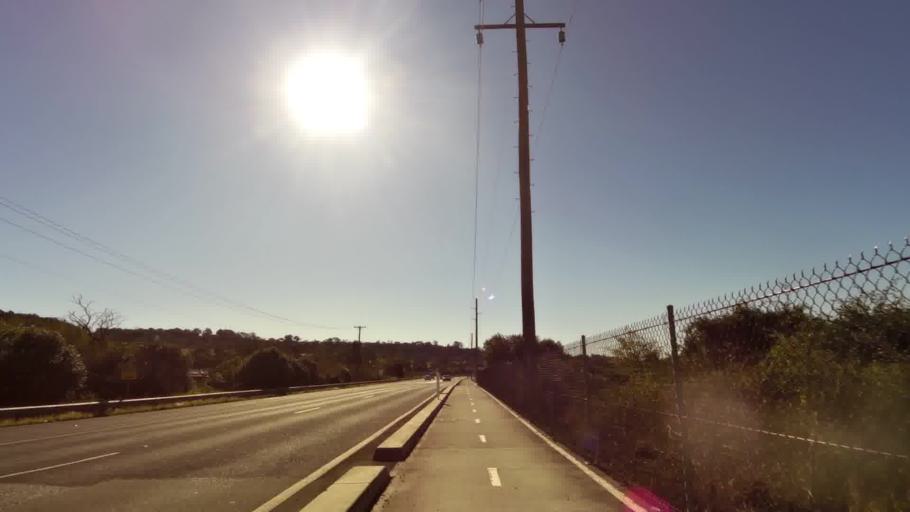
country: AU
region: New South Wales
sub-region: Wollongong
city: Koonawarra
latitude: -34.4729
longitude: 150.8151
